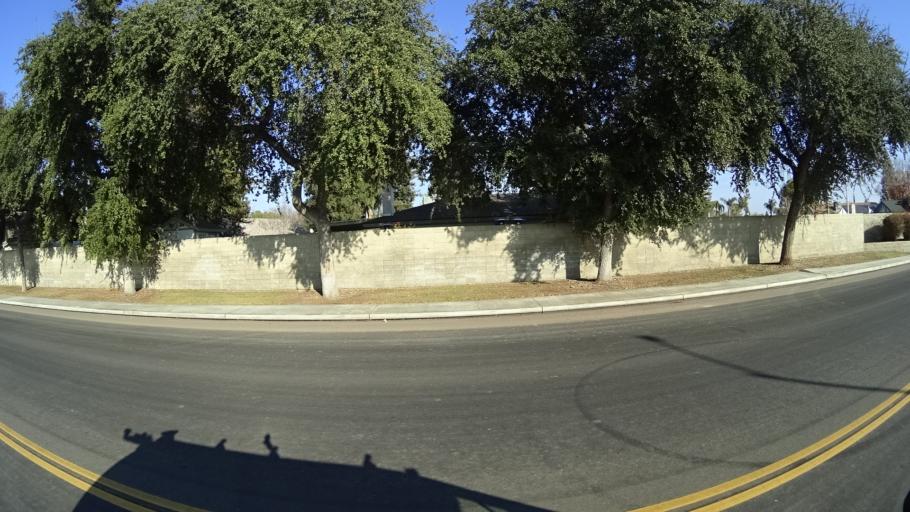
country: US
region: California
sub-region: Kern County
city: Greenacres
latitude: 35.3229
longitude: -119.0987
